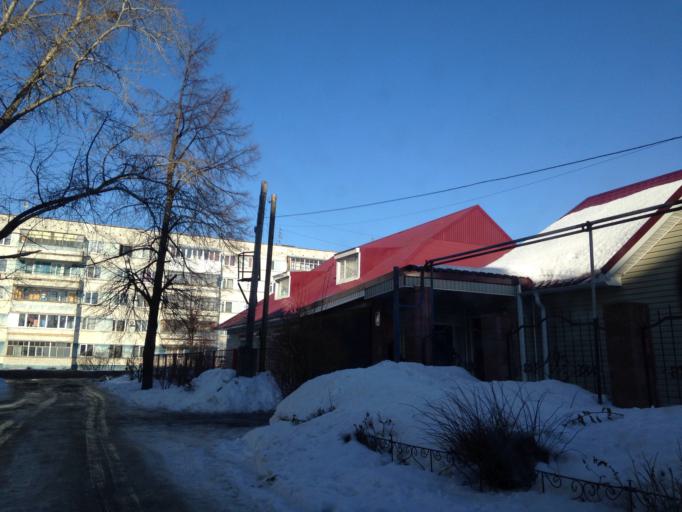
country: RU
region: Ulyanovsk
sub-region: Ulyanovskiy Rayon
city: Ulyanovsk
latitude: 54.2918
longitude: 48.3187
